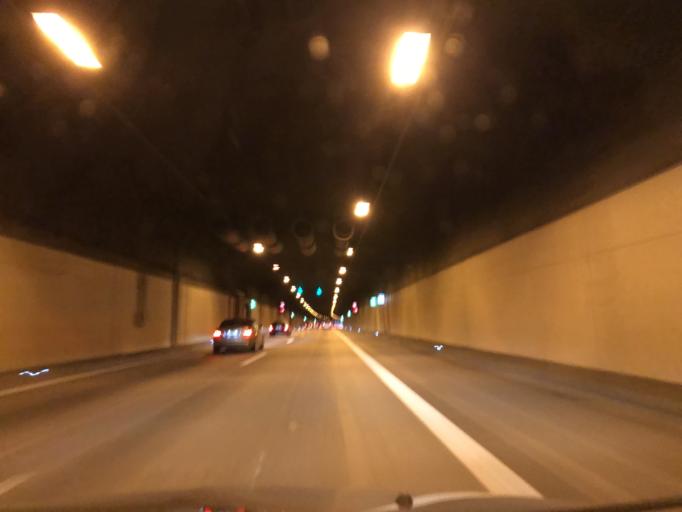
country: DE
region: Baden-Wuerttemberg
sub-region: Regierungsbezirk Stuttgart
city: Fellbach
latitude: 48.8000
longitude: 9.2747
